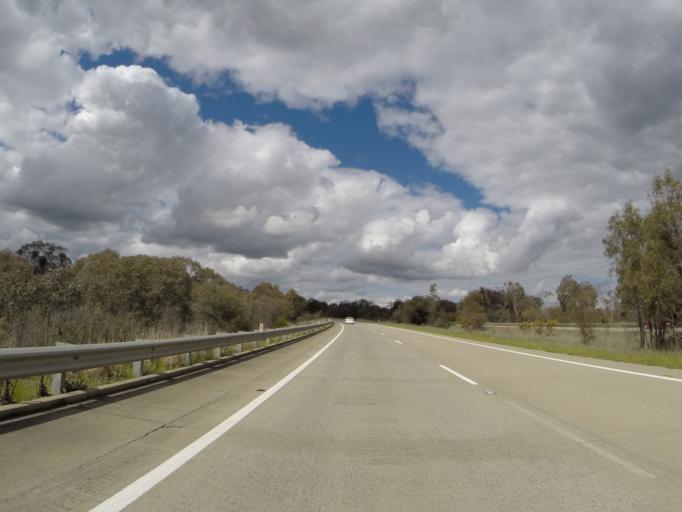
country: AU
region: New South Wales
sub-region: Yass Valley
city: Gundaroo
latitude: -34.7896
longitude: 149.2151
